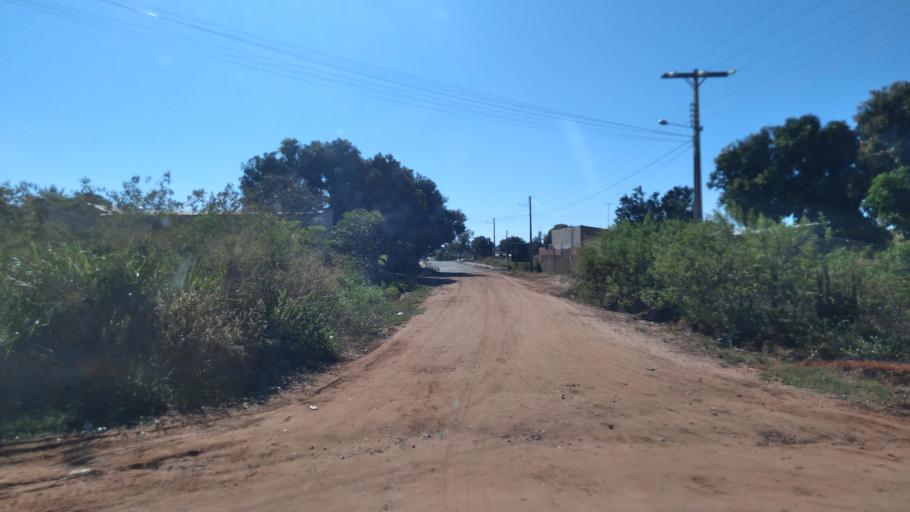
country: BR
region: Goias
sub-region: Mineiros
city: Mineiros
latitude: -17.5918
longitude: -52.5554
